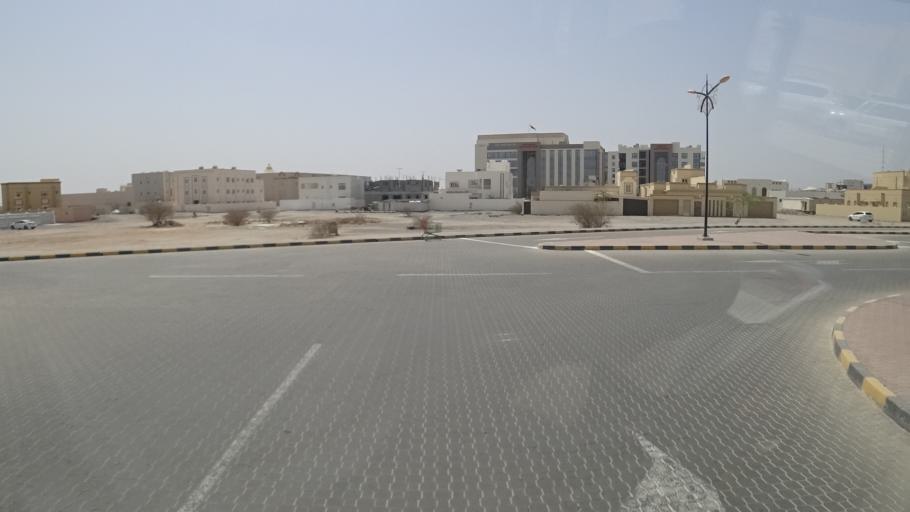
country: OM
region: Muhafazat ad Dakhiliyah
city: Nizwa
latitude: 22.8747
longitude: 57.5392
